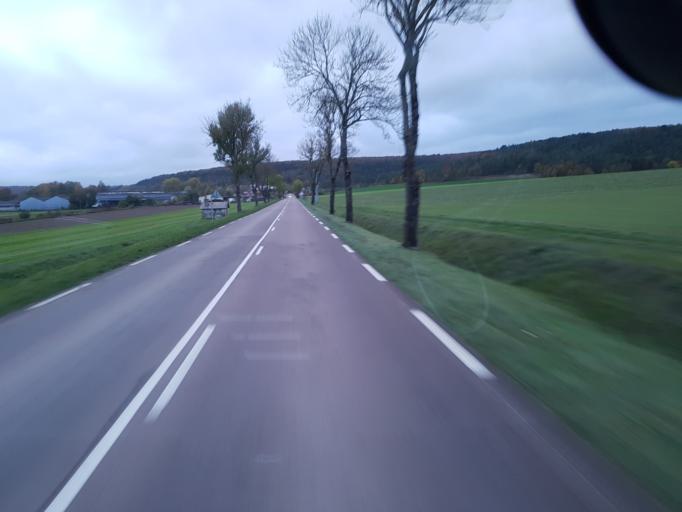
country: FR
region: Champagne-Ardenne
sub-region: Departement de l'Aube
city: Mussy-sur-Seine
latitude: 47.9880
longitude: 4.4847
